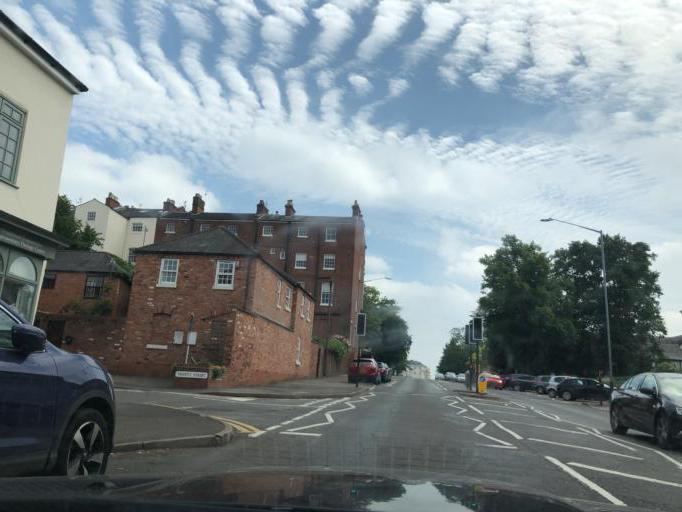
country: GB
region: England
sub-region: Warwickshire
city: Royal Leamington Spa
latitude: 52.2956
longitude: -1.5401
